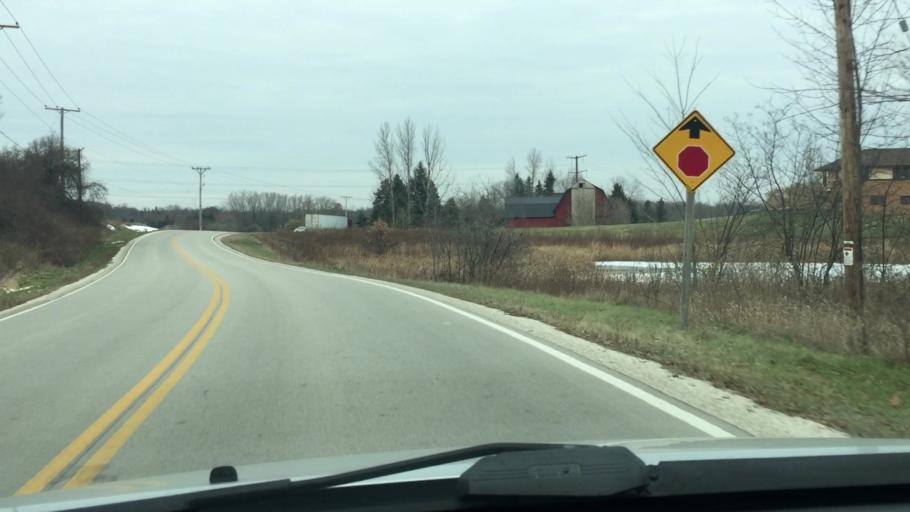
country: US
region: Wisconsin
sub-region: Ozaukee County
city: Cedarburg
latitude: 43.2761
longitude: -87.9727
